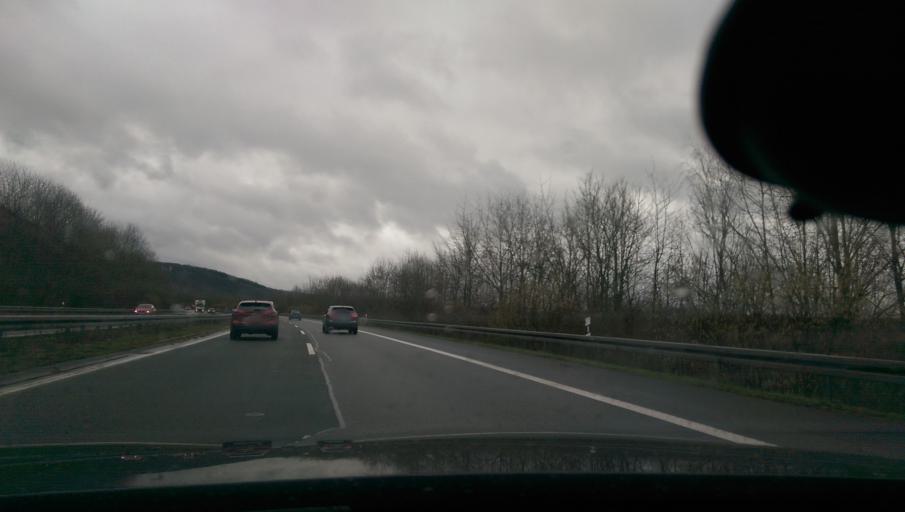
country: DE
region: North Rhine-Westphalia
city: Wickede
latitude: 51.4728
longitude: 7.9353
